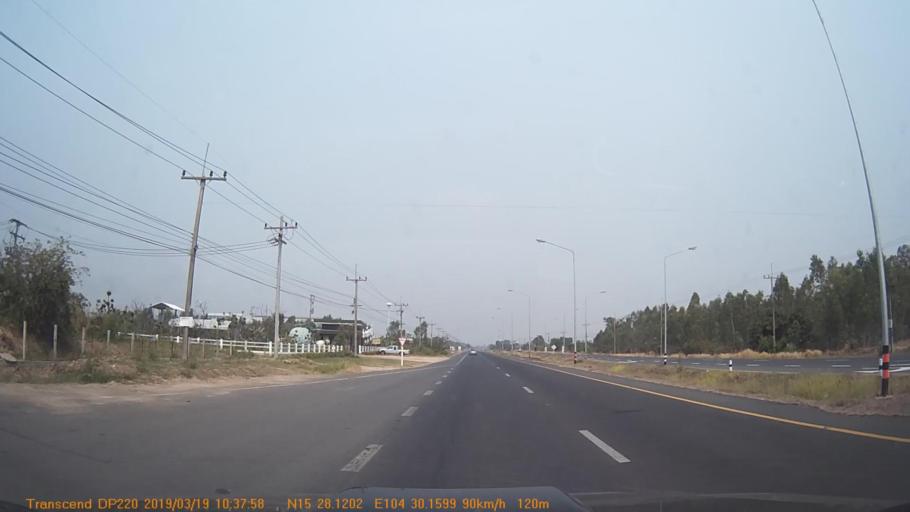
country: TH
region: Changwat Ubon Ratchathani
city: Khueang Nai
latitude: 15.4689
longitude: 104.5025
